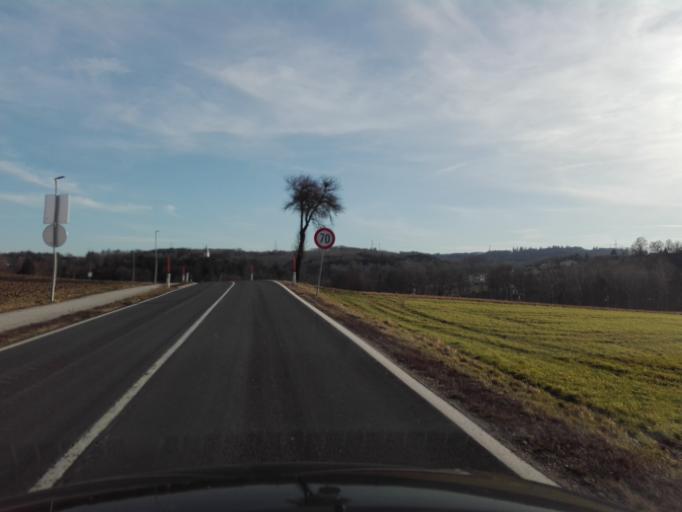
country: AT
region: Lower Austria
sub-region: Politischer Bezirk Amstetten
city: Amstetten
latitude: 48.1668
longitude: 14.8397
